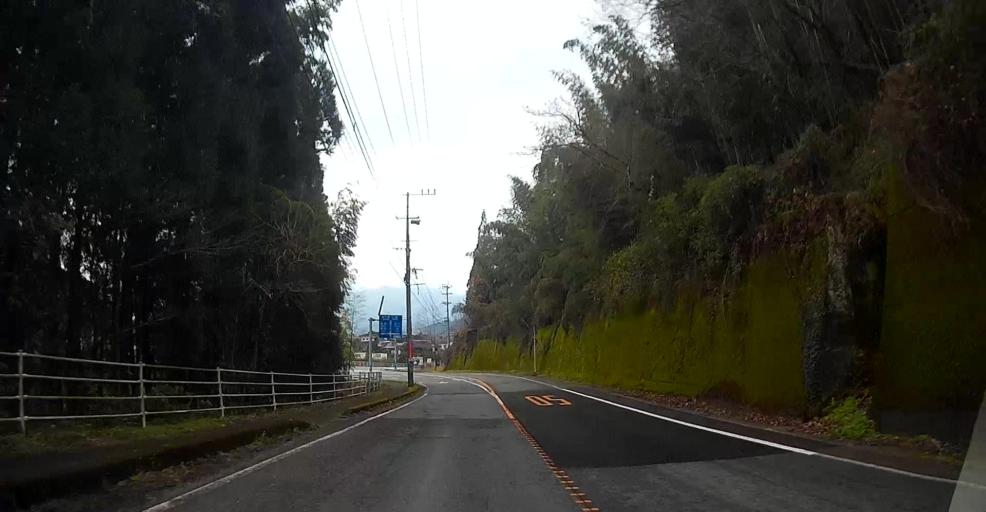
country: JP
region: Kumamoto
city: Matsubase
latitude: 32.6269
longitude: 130.8117
